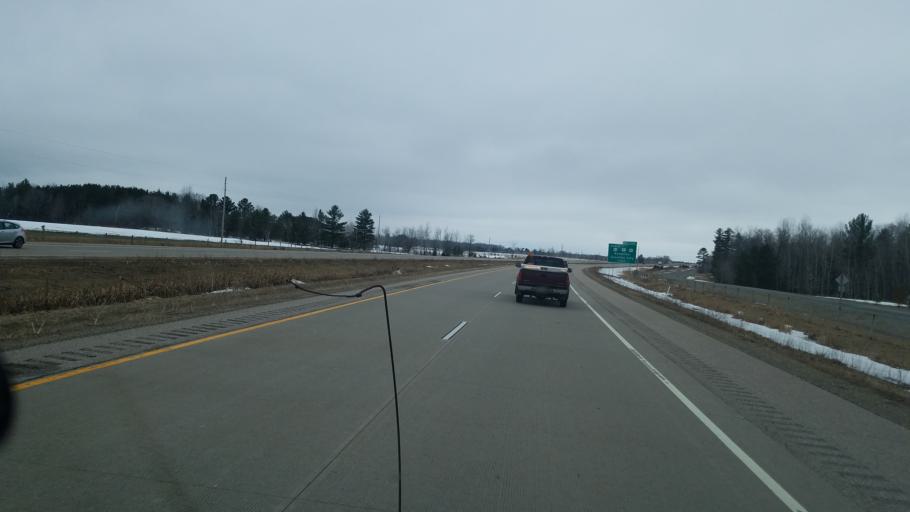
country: US
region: Wisconsin
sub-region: Portage County
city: Stevens Point
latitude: 44.5988
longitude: -89.6907
